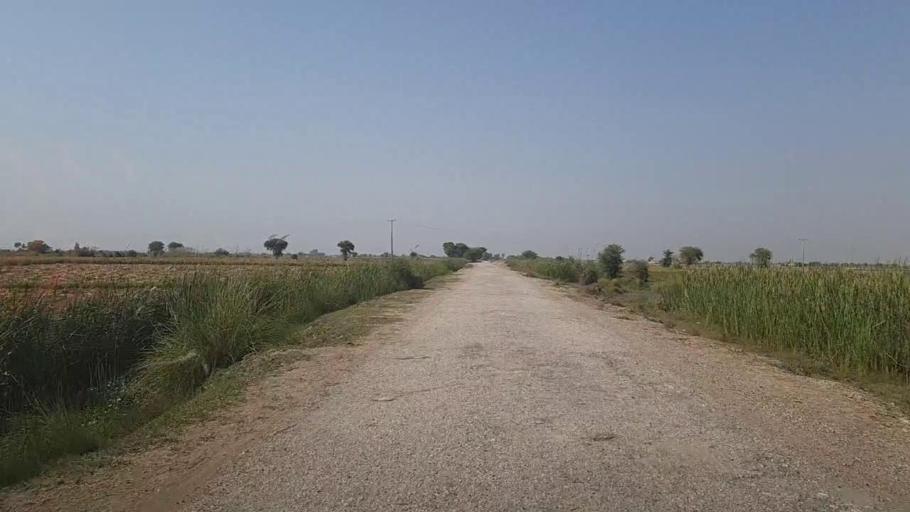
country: PK
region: Sindh
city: Kandhkot
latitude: 28.4002
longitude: 69.2646
